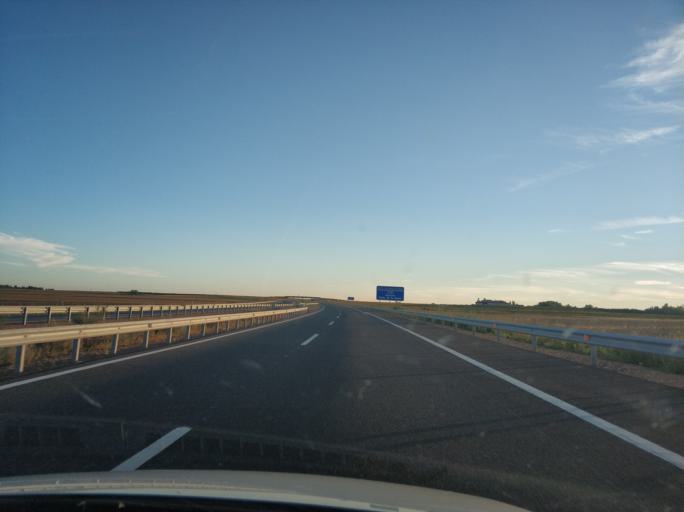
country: ES
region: Castille and Leon
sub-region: Provincia de Zamora
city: Castrogonzalo
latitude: 41.9600
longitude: -5.6109
